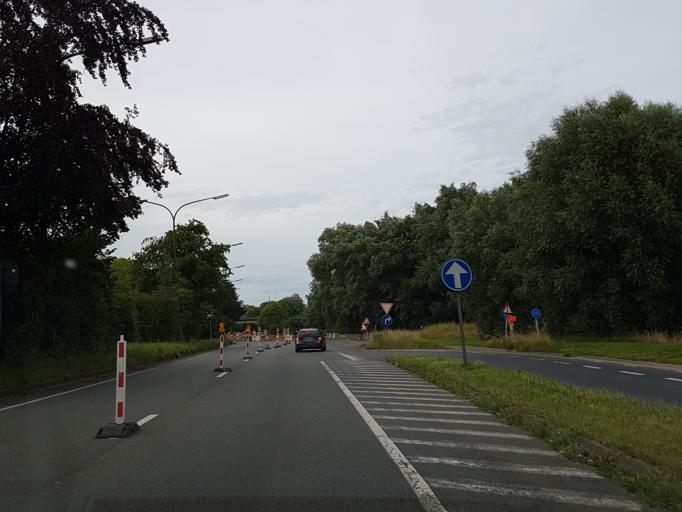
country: BE
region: Flanders
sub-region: Provincie Vlaams-Brabant
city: Kraainem
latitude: 50.8609
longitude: 4.4506
